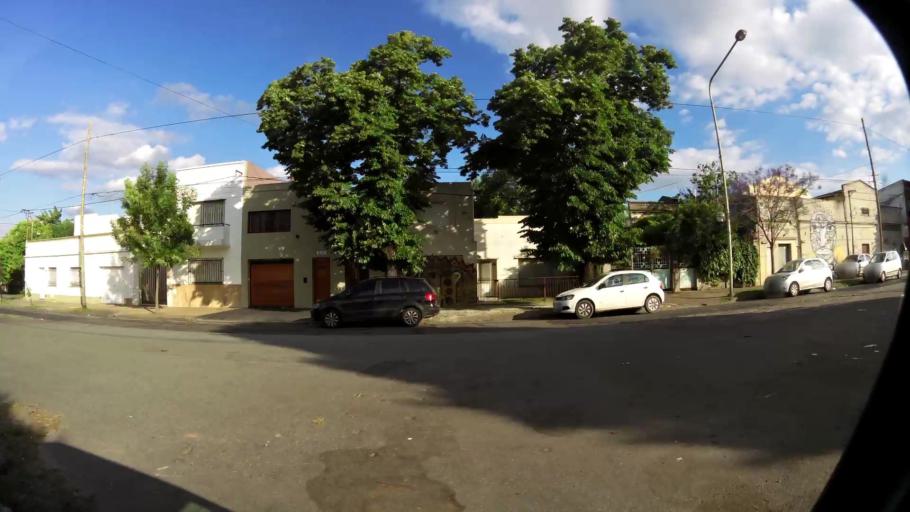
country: AR
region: Buenos Aires
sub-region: Partido de La Plata
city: La Plata
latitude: -34.8975
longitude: -57.9533
